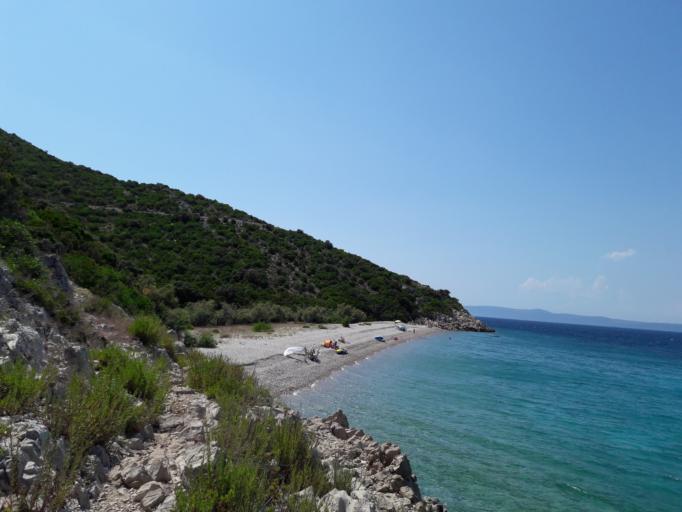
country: HR
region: Dubrovacko-Neretvanska
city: Orebic
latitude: 43.0233
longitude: 17.1580
